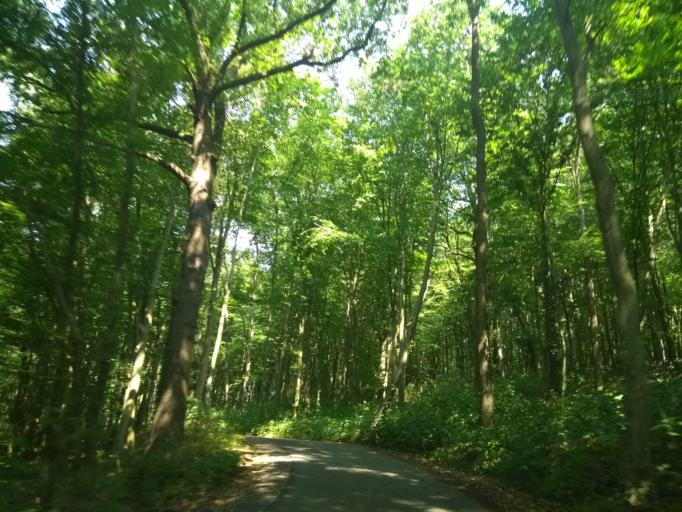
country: DE
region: Thuringia
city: Eisenberg
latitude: 50.9770
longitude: 11.9094
